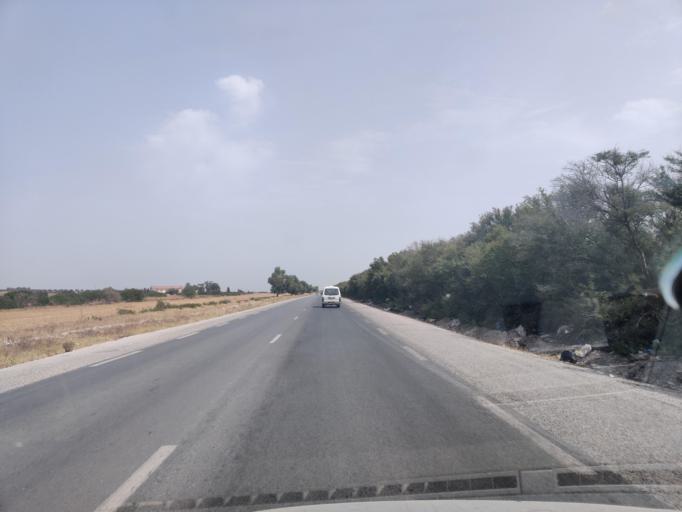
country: TN
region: Nabul
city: Bu `Urqub
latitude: 36.4849
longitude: 10.5719
